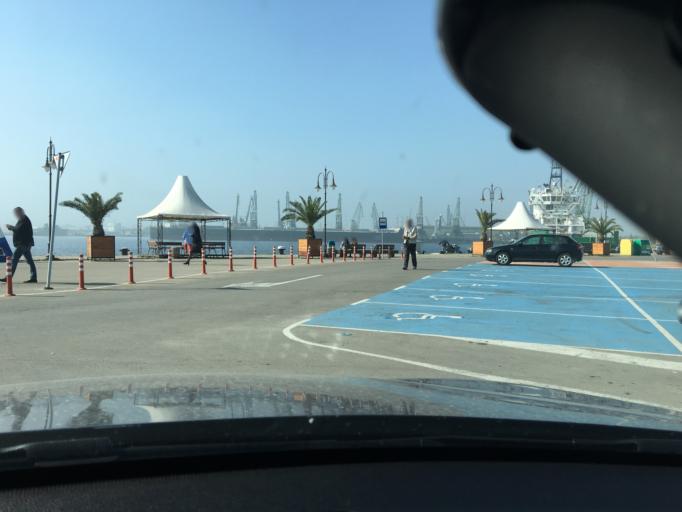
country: BG
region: Varna
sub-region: Obshtina Varna
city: Varna
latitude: 43.1956
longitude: 27.9209
